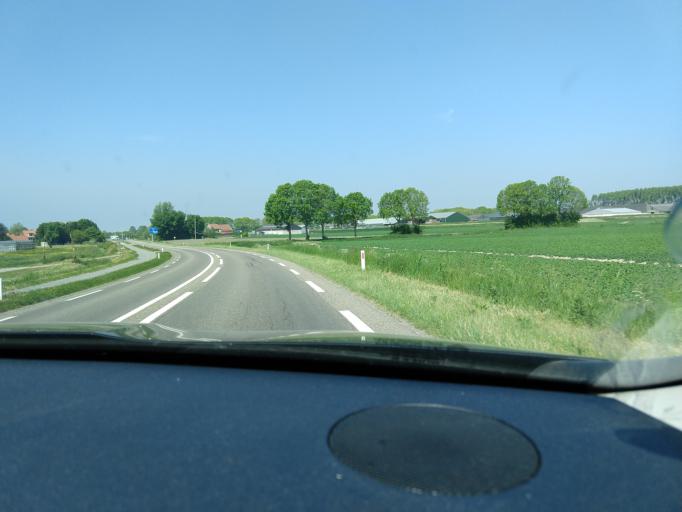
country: NL
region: Zeeland
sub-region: Gemeente Reimerswaal
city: Yerseke
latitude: 51.5499
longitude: 4.1103
